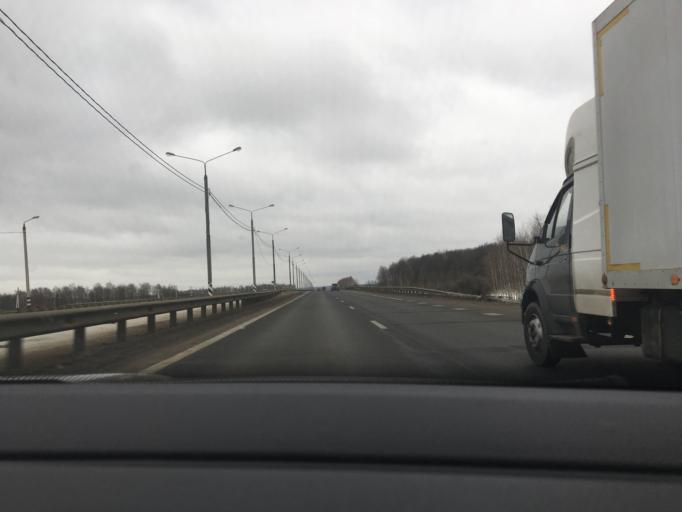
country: RU
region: Tula
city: Zaokskiy
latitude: 54.8029
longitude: 37.4843
